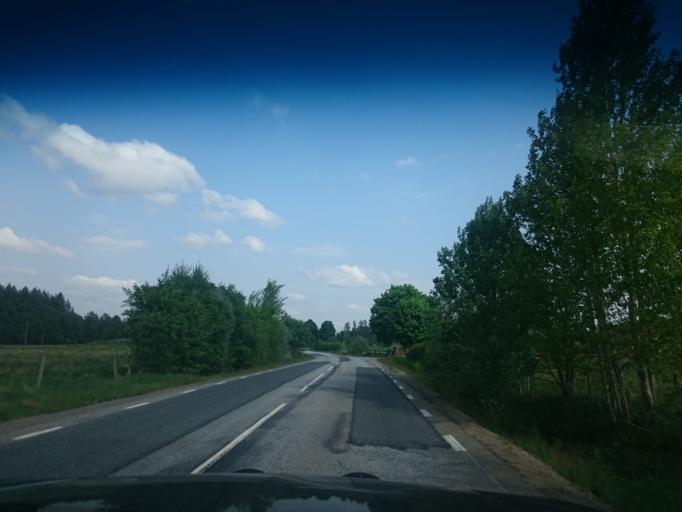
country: SE
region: Joenkoeping
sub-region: Vetlanda Kommun
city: Landsbro
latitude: 57.3810
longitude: 14.9738
